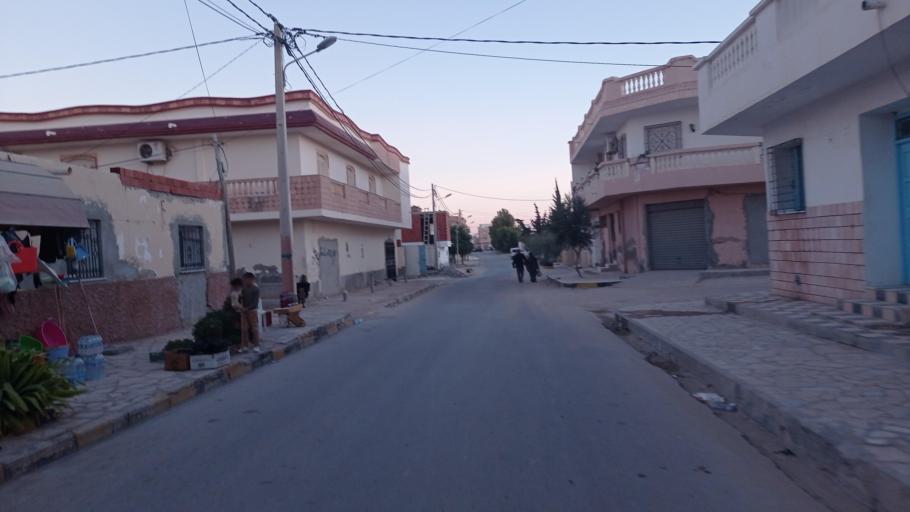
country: TN
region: Qabis
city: Gabes
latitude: 33.8462
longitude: 10.1149
